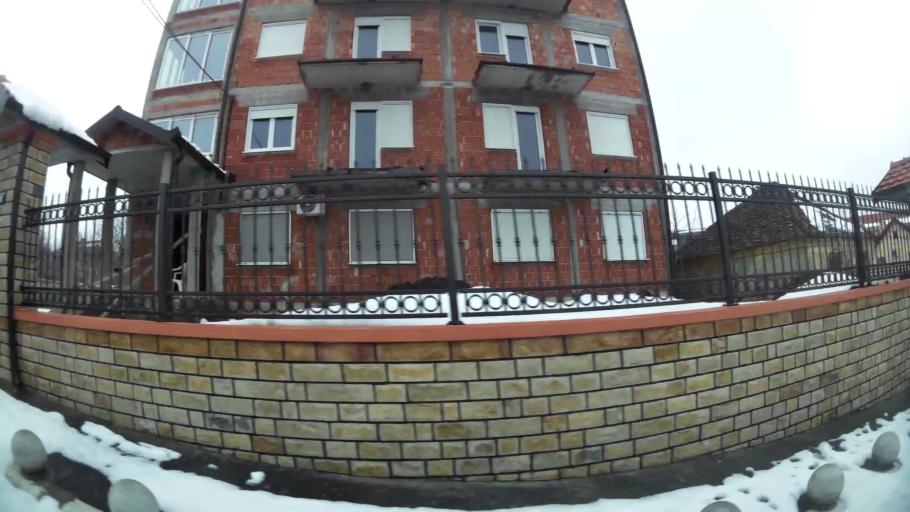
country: RS
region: Central Serbia
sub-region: Belgrade
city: Zvezdara
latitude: 44.7636
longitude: 20.5158
